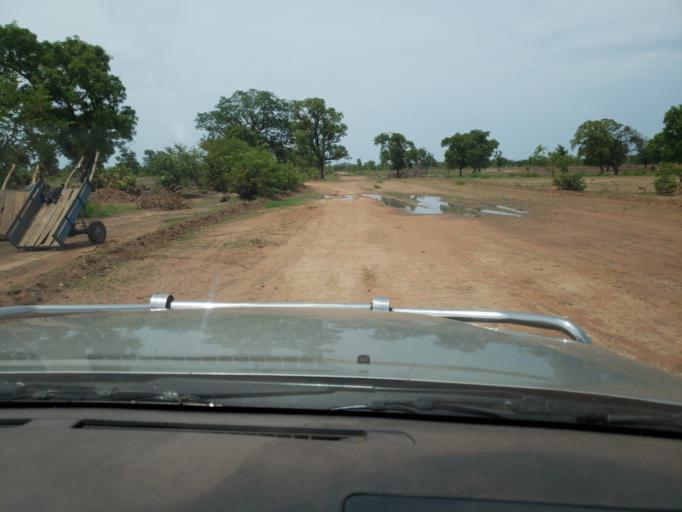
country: ML
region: Koulikoro
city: Kolokani
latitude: 13.4895
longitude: -8.2437
